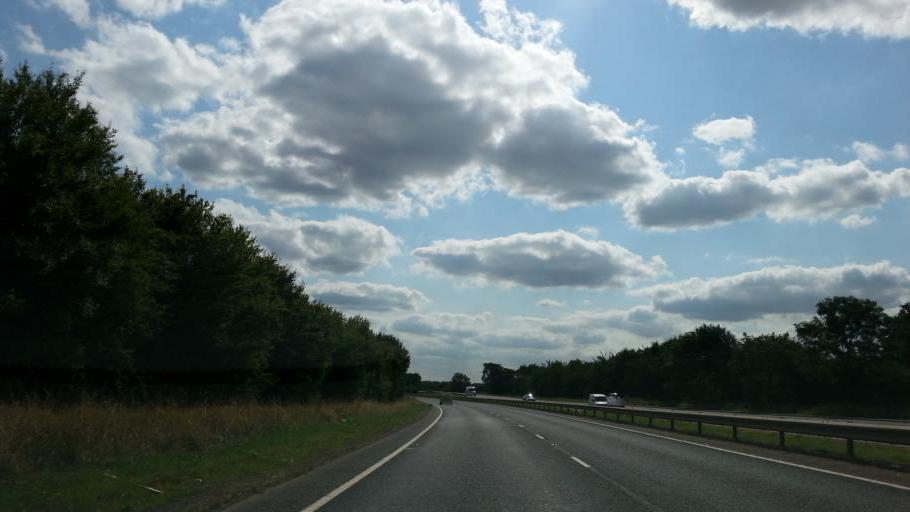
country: GB
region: England
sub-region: Leicestershire
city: Mountsorrel
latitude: 52.7041
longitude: -1.1264
